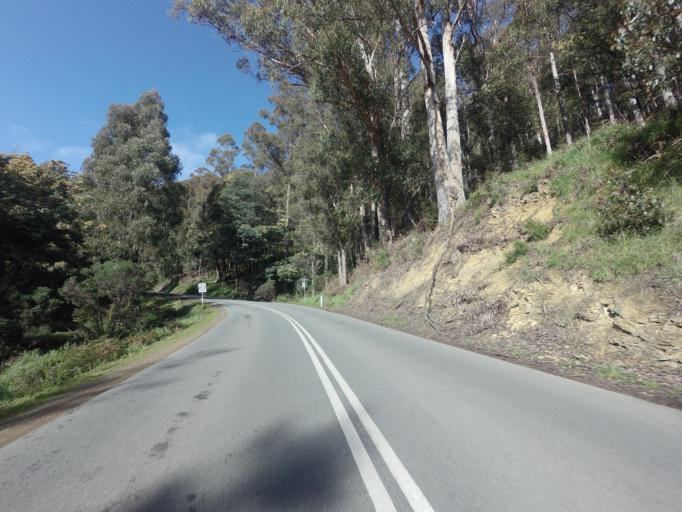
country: AU
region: Tasmania
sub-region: Huon Valley
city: Geeveston
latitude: -43.2487
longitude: 146.9905
